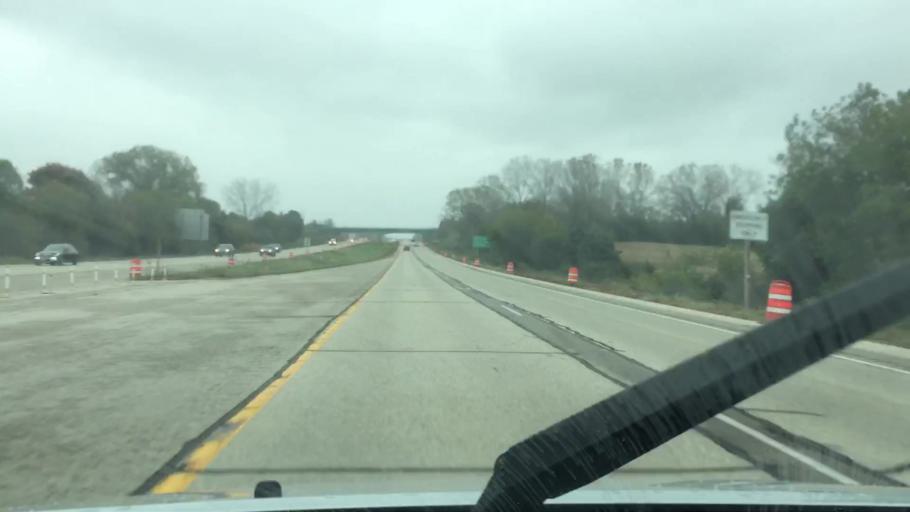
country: US
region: Wisconsin
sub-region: Walworth County
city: Lake Geneva
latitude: 42.5835
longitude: -88.3967
